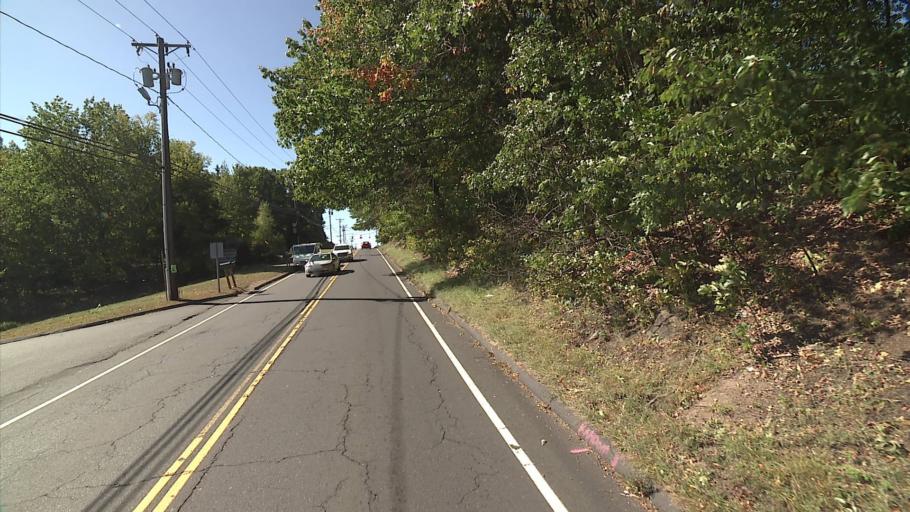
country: US
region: Connecticut
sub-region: New Haven County
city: Wolcott
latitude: 41.5941
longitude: -72.9879
